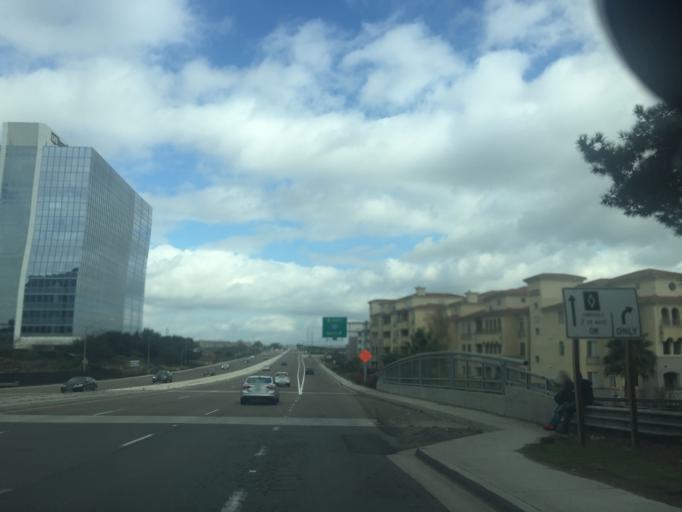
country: US
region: California
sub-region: San Diego County
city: La Jolla
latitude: 32.8741
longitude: -117.2057
